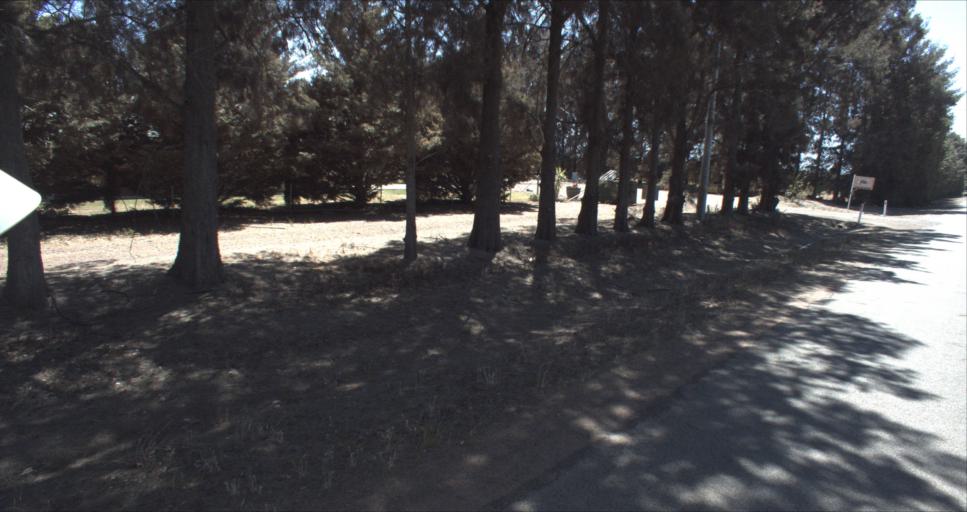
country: AU
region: New South Wales
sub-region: Leeton
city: Leeton
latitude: -34.5290
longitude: 146.3294
